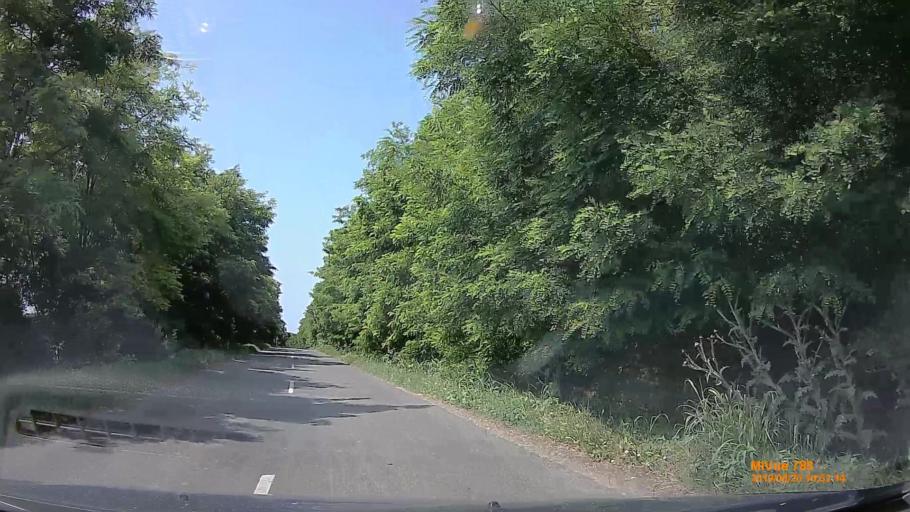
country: HU
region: Baranya
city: Mecseknadasd
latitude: 46.1580
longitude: 18.5811
